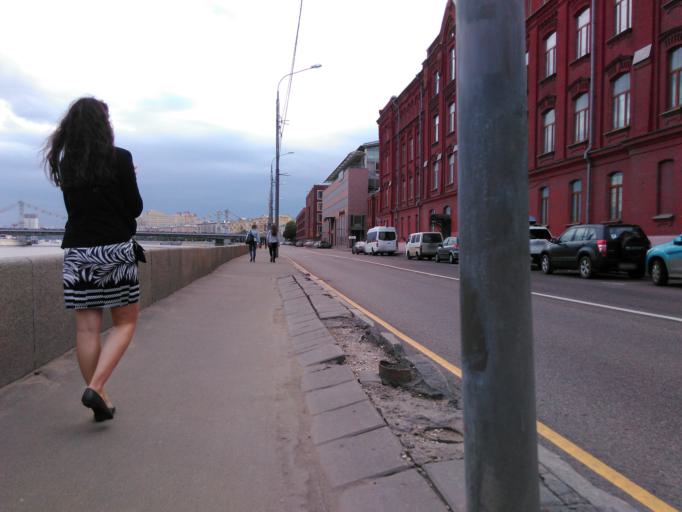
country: RU
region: Moscow
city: Moscow
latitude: 55.7379
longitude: 37.6042
